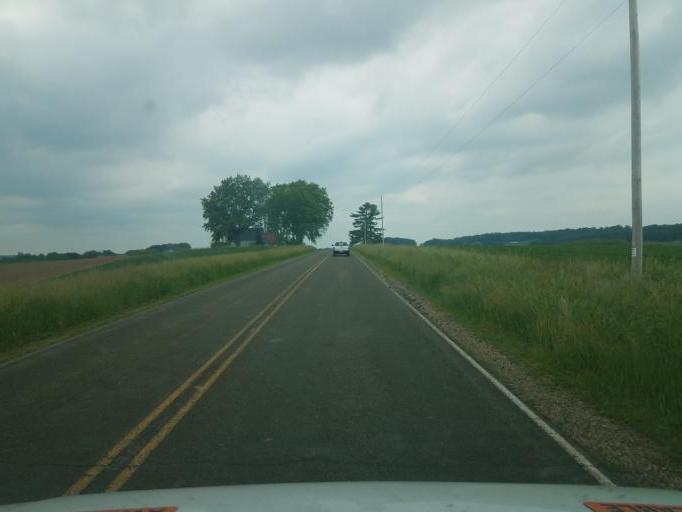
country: US
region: Wisconsin
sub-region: Juneau County
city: Elroy
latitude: 43.6526
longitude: -90.2470
